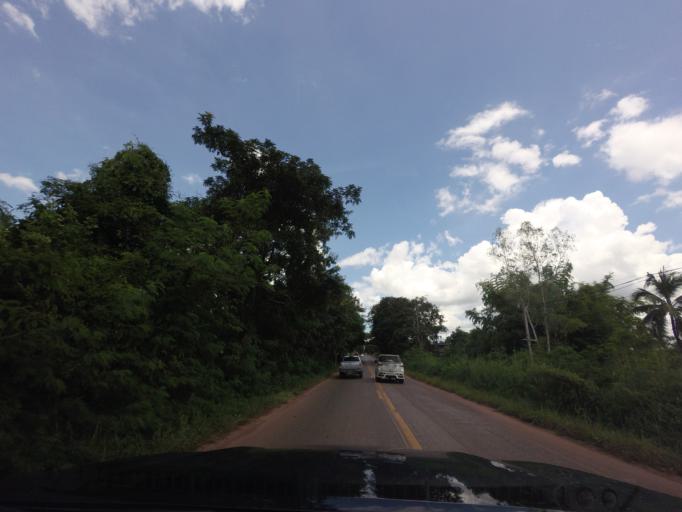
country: TH
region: Changwat Udon Thani
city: Ban Dung
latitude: 17.6561
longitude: 103.1433
